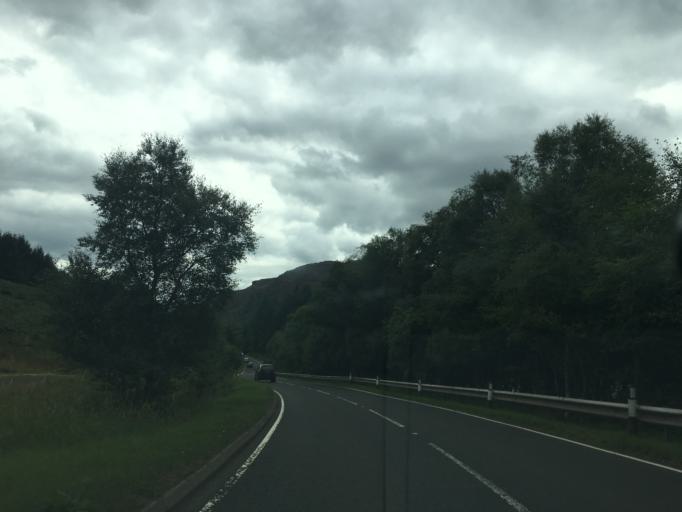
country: GB
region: Scotland
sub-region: Stirling
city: Callander
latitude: 56.4237
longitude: -4.3385
